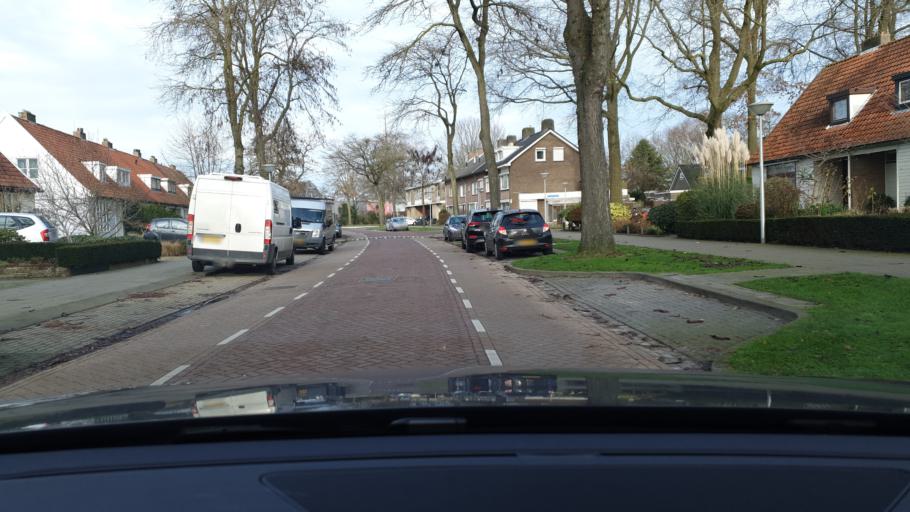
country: NL
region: North Brabant
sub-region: Gemeente Eindhoven
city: De Doornakkers
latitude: 51.4411
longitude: 5.5145
